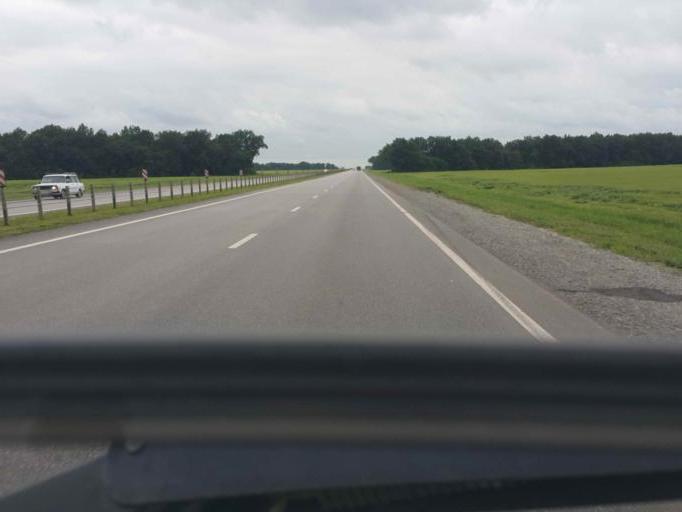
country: RU
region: Tambov
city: Zavoronezhskoye
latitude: 52.8944
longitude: 40.6848
